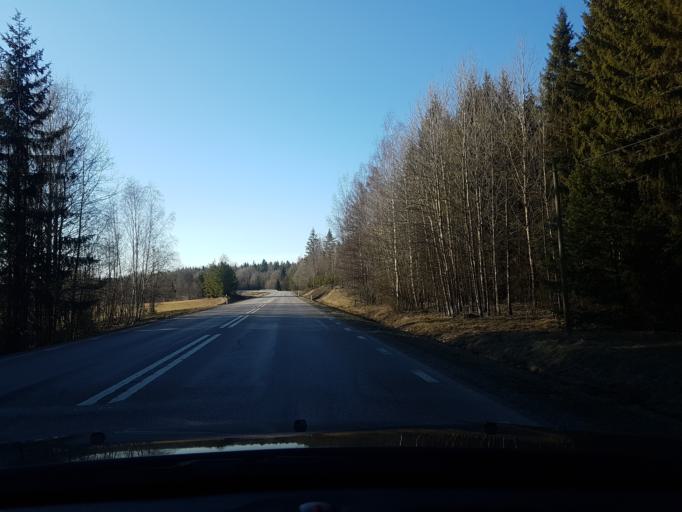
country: SE
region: Uppsala
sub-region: Heby Kommun
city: Morgongava
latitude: 59.9140
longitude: 17.0276
